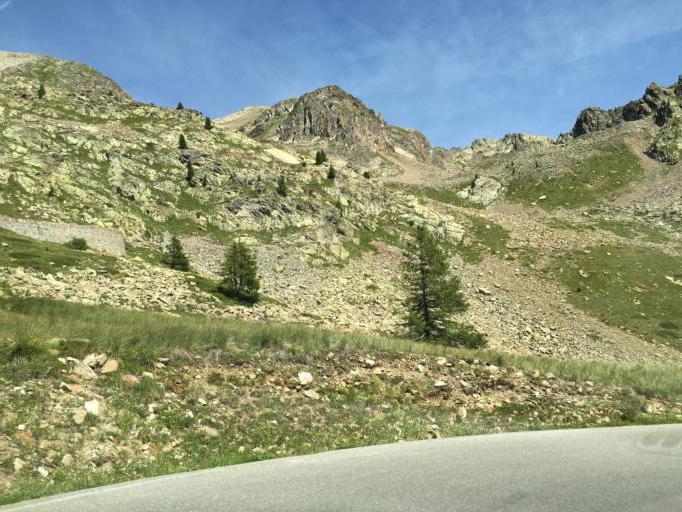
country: IT
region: Piedmont
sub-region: Provincia di Cuneo
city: Vinadio
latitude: 44.1993
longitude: 7.1552
